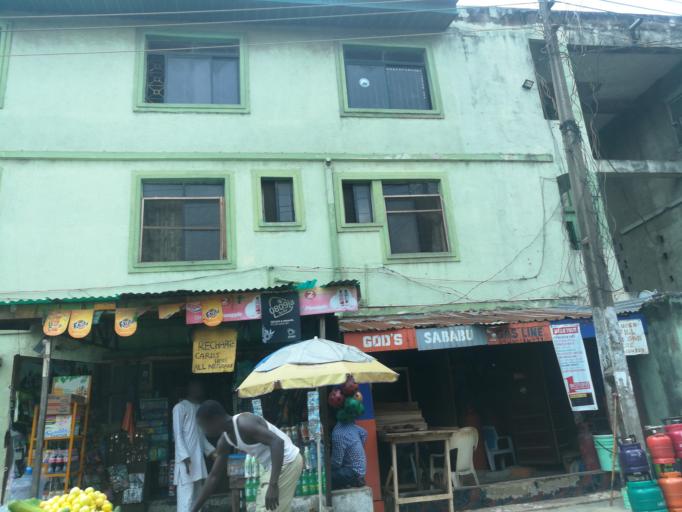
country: NG
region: Lagos
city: Somolu
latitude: 6.5362
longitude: 3.3645
